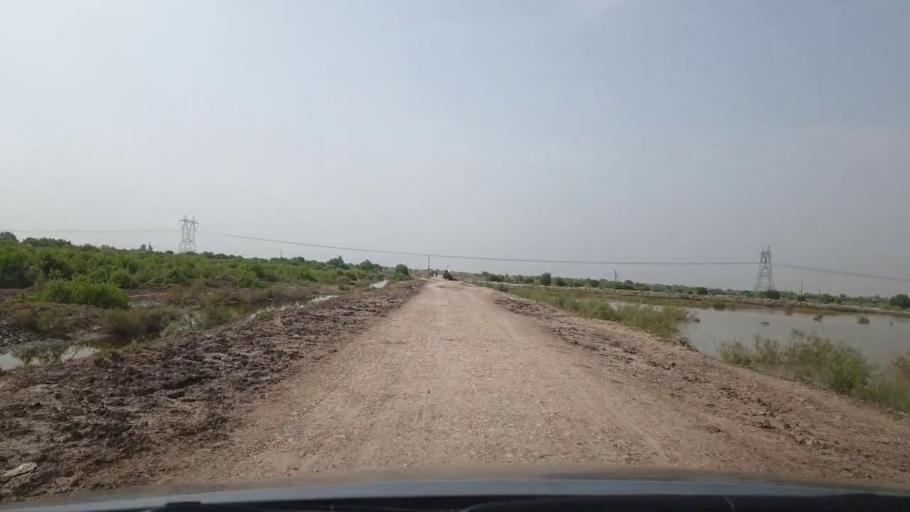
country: PK
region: Sindh
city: Rohri
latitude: 27.6781
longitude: 69.0117
